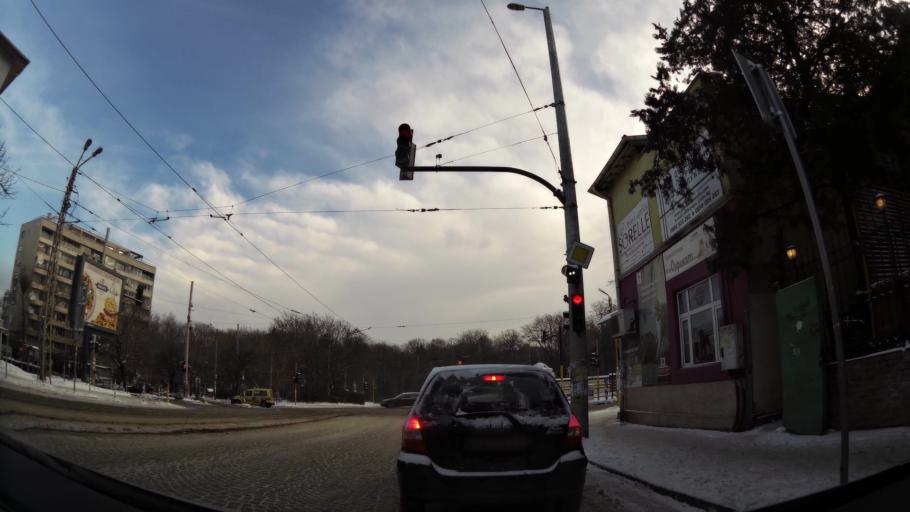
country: BG
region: Sofia-Capital
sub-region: Stolichna Obshtina
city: Sofia
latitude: 42.6761
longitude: 23.3334
